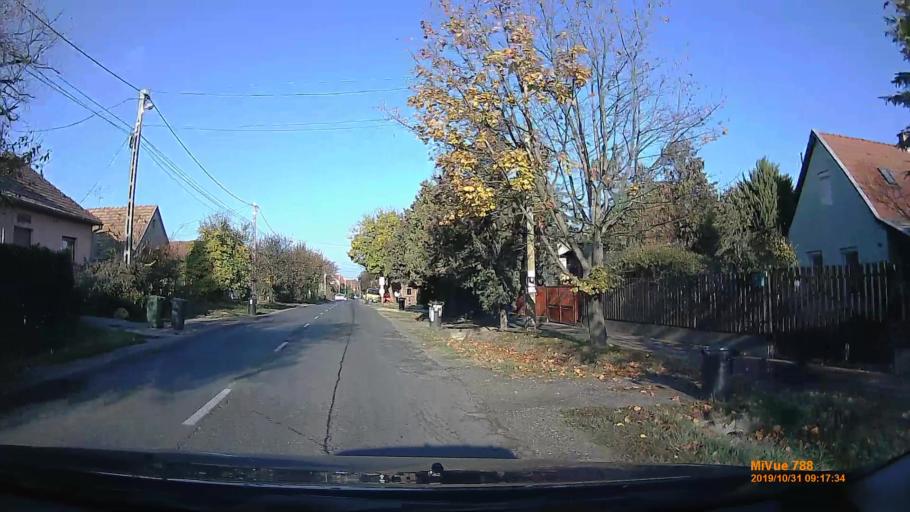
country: HU
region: Pest
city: Gyomro
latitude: 47.4088
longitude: 19.4038
